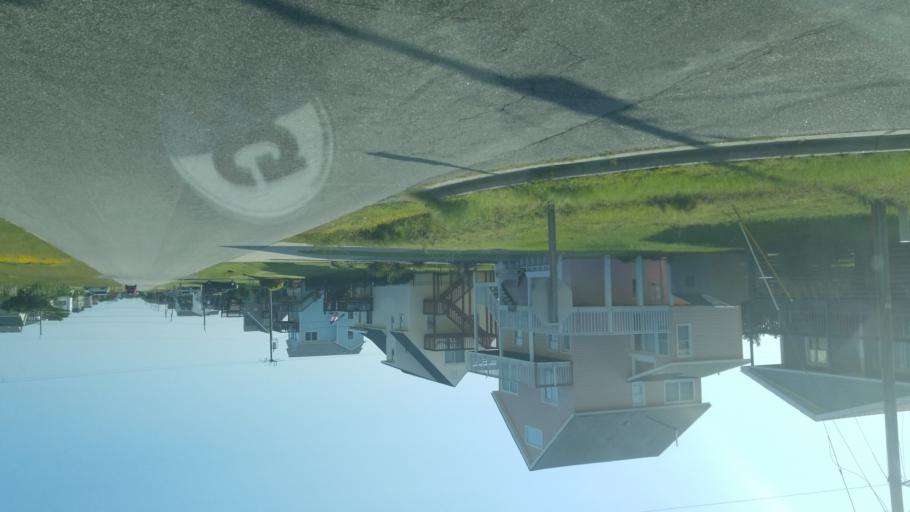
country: US
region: North Carolina
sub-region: Dare County
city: Kill Devil Hills
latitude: 36.0128
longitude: -75.6580
